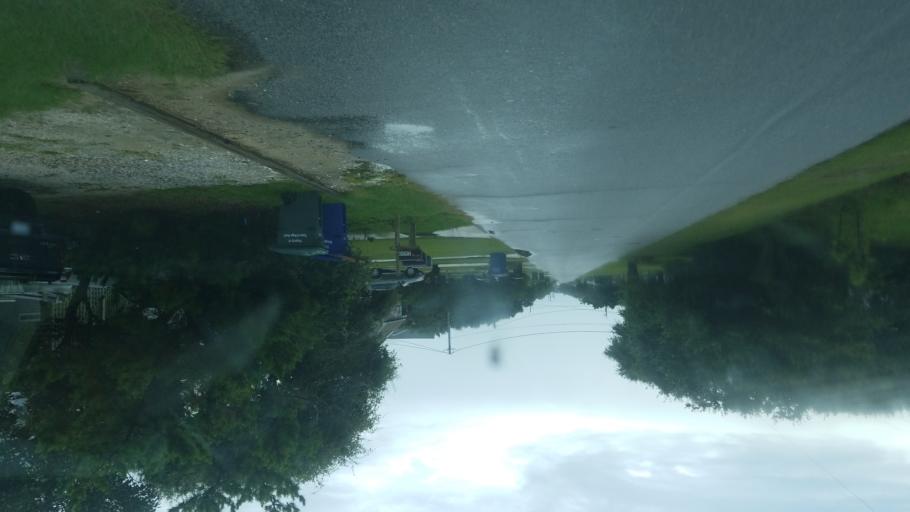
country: US
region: North Carolina
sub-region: Dare County
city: Nags Head
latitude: 35.9810
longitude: -75.6402
